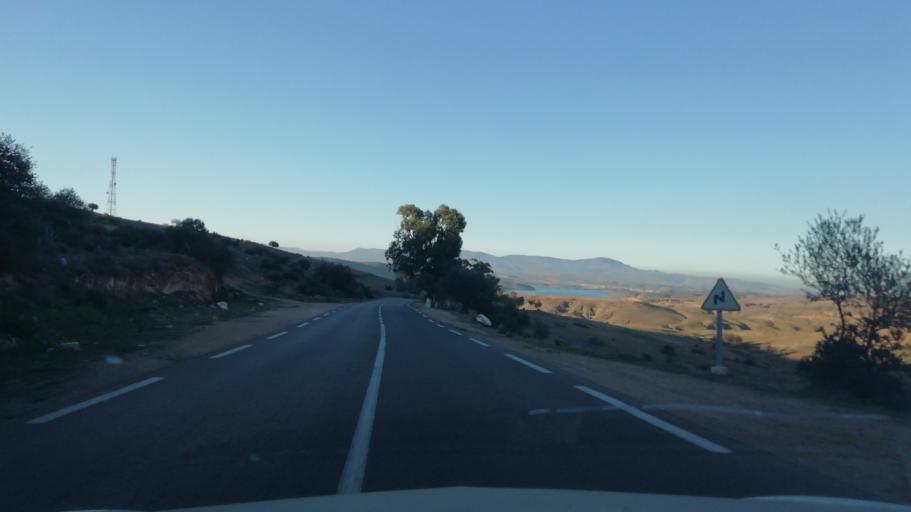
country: DZ
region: Tlemcen
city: Beni Mester
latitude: 34.8235
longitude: -1.6377
